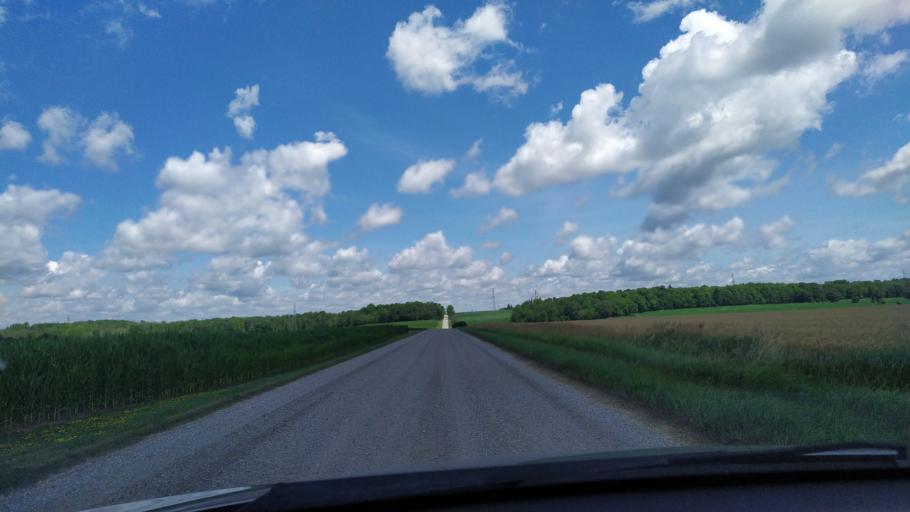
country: CA
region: Ontario
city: Stratford
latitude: 43.3698
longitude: -80.7615
